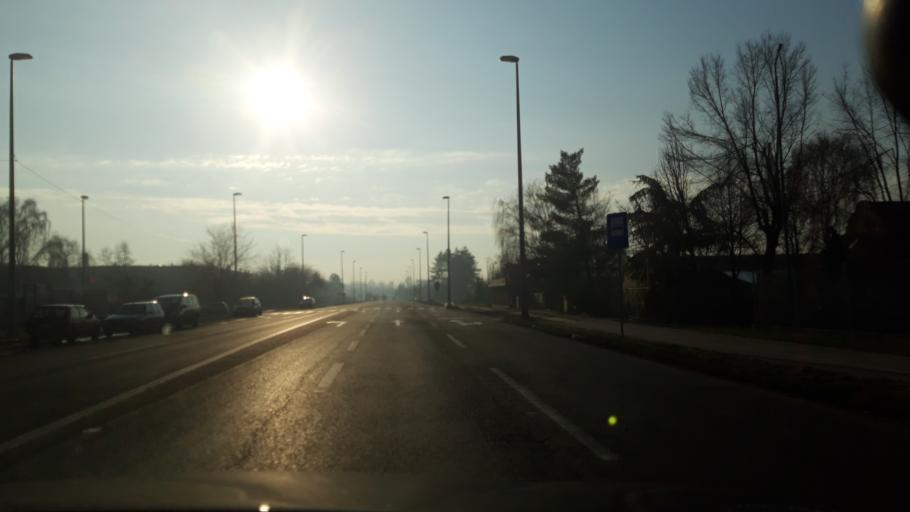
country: RS
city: Pocerski Pricinovic
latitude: 44.7445
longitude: 19.7203
